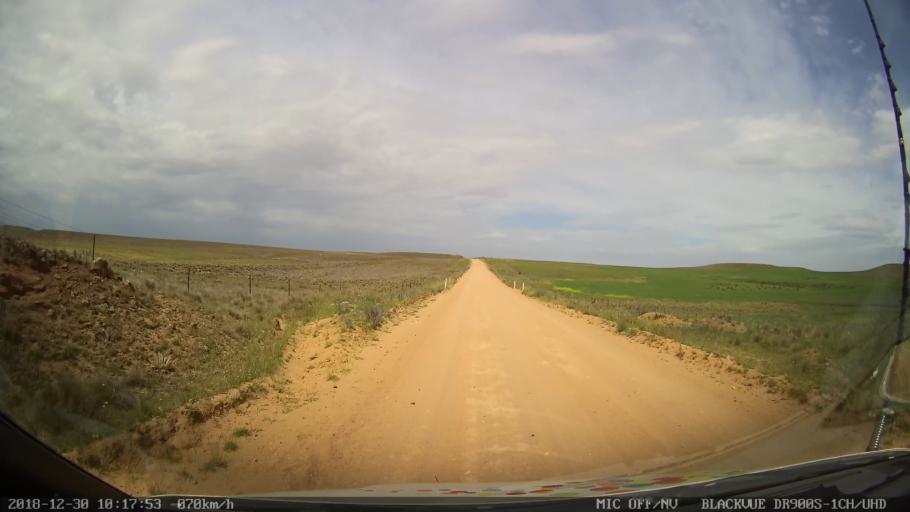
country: AU
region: New South Wales
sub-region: Snowy River
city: Berridale
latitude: -36.5499
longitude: 149.0155
